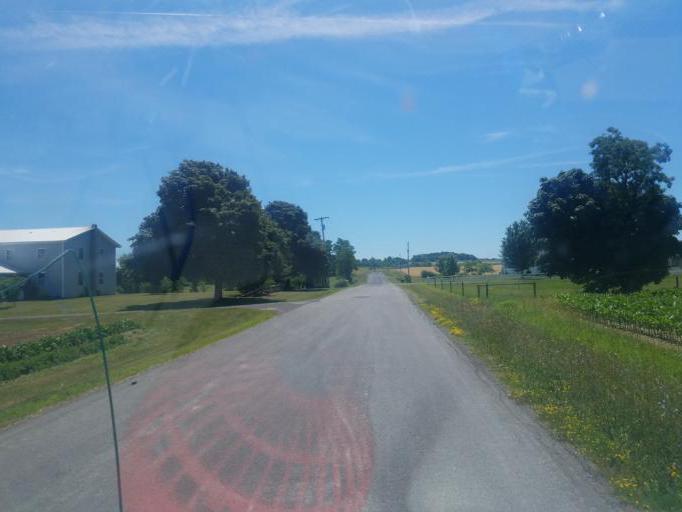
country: US
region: New York
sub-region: Yates County
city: Penn Yan
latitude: 42.6446
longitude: -77.0175
